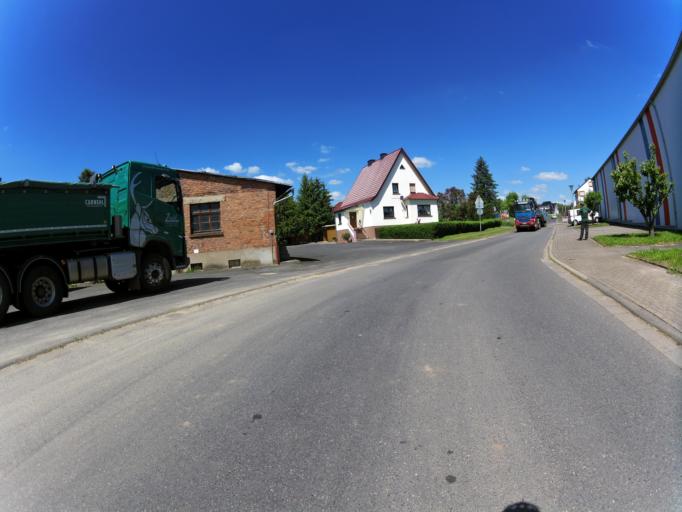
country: DE
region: Thuringia
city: Dankmarshausen
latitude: 50.9511
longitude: 10.0223
